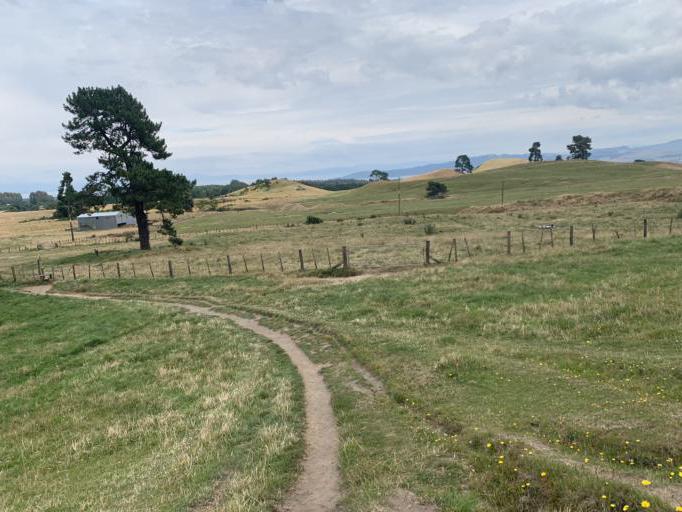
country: NZ
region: Waikato
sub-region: Taupo District
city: Taupo
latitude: -38.7033
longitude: 176.1410
